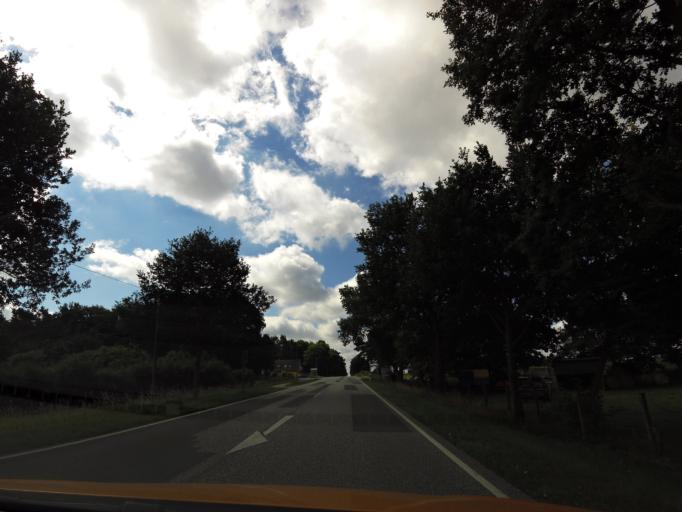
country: DE
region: Mecklenburg-Vorpommern
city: Plau am See
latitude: 53.5046
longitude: 12.2665
